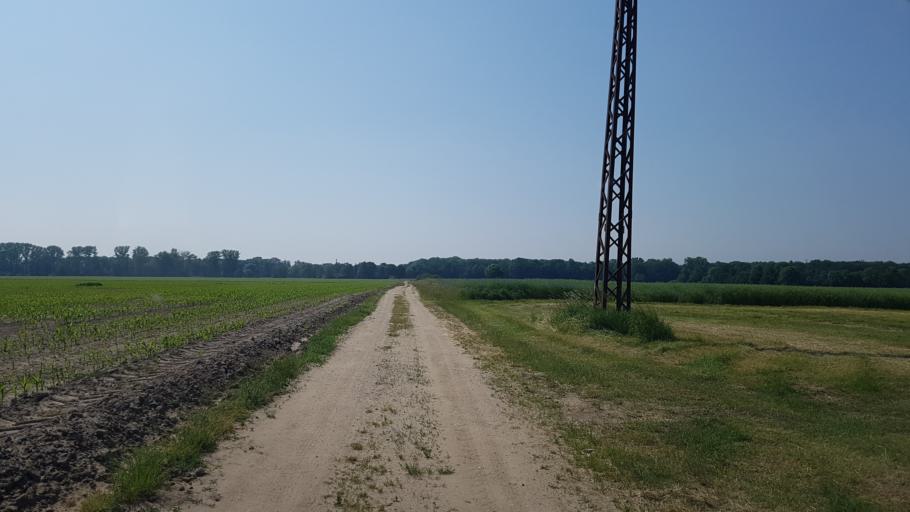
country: DE
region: Brandenburg
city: Sonnewalde
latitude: 51.7116
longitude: 13.6420
